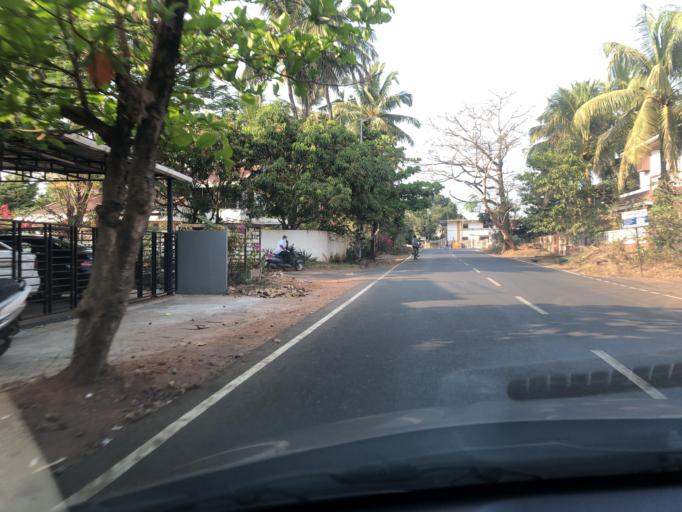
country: IN
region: Goa
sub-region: North Goa
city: Serula
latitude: 15.5297
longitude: 73.8289
